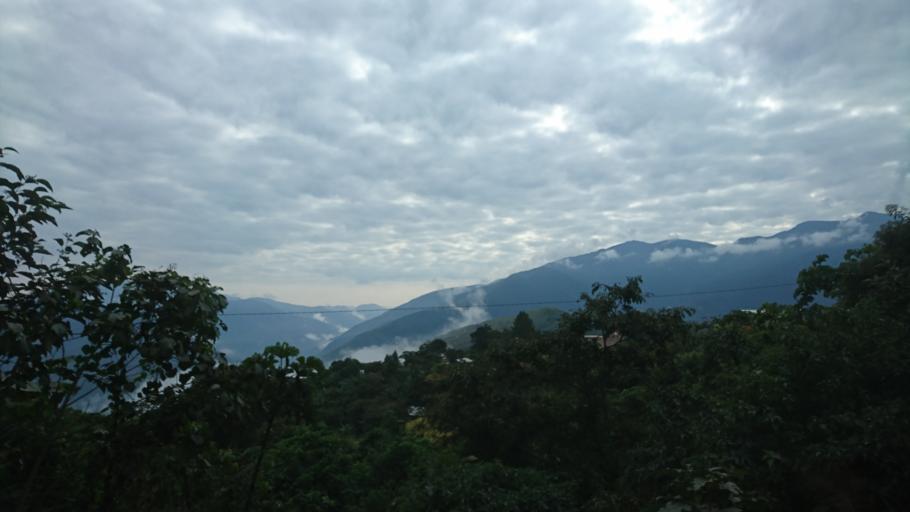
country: BO
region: La Paz
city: Coroico
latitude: -16.1905
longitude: -67.7126
